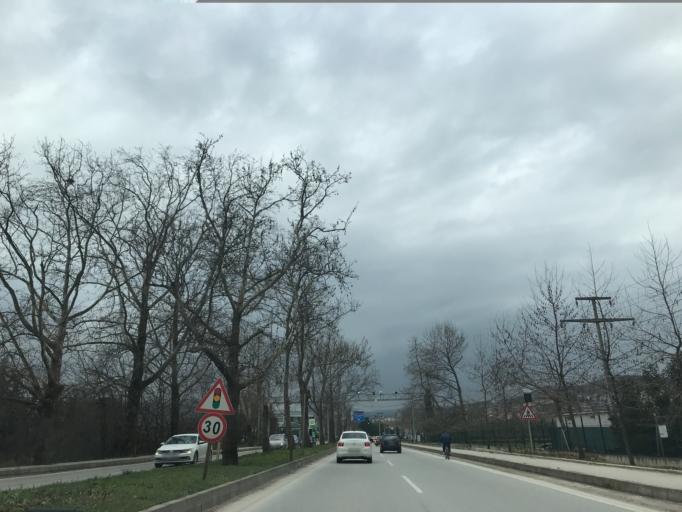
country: TR
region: Yalova
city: Kadikoy
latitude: 40.6469
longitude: 29.2352
